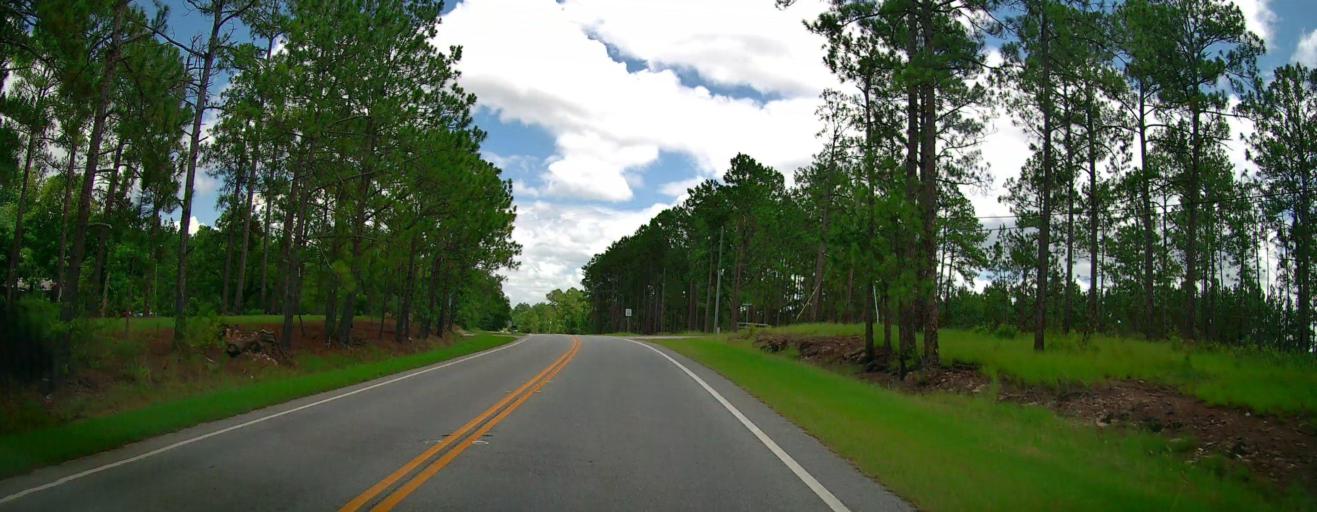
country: US
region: Georgia
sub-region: Turner County
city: Ashburn
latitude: 31.7227
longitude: -83.5813
